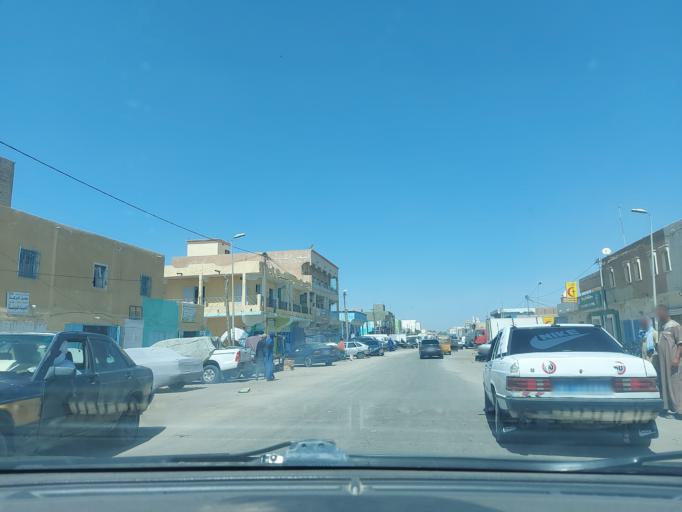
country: MR
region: Nouakchott
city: Nouakchott
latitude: 18.0816
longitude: -15.9775
